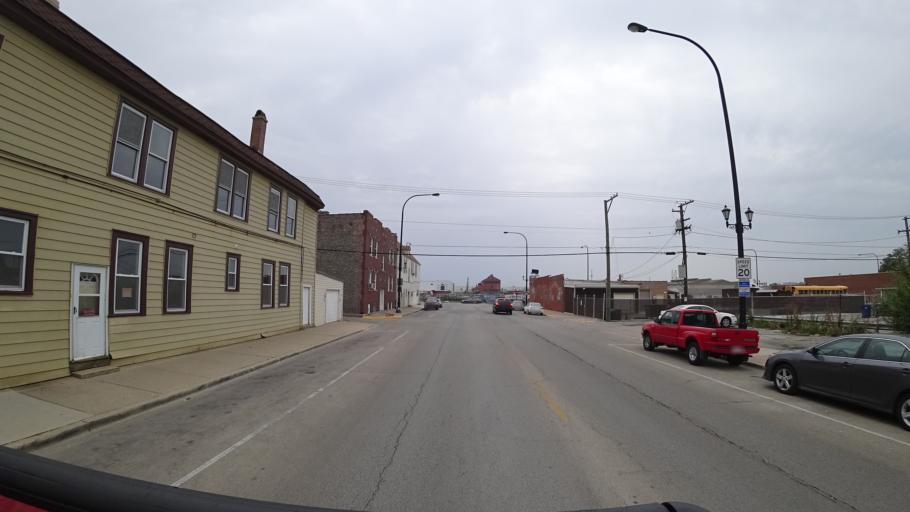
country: US
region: Illinois
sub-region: Cook County
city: Cicero
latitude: 41.8621
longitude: -87.7535
